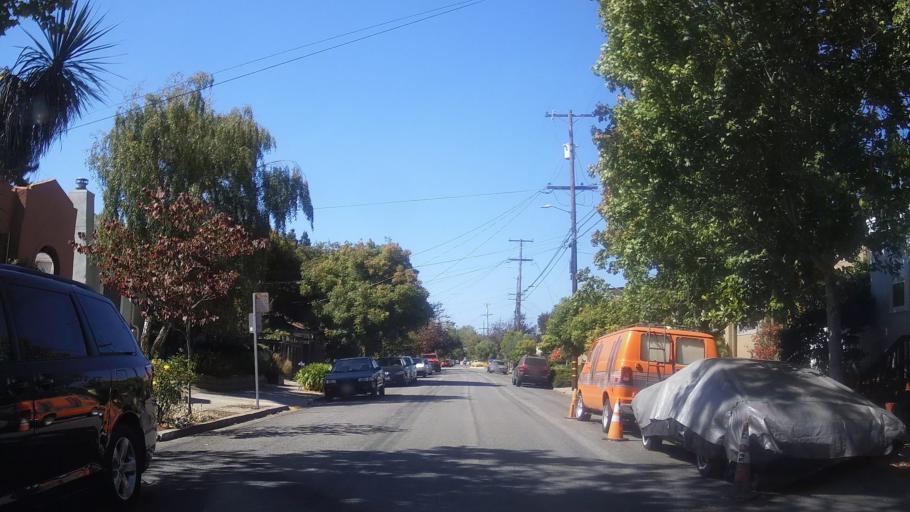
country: US
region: California
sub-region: Alameda County
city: Albany
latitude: 37.8771
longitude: -122.2918
